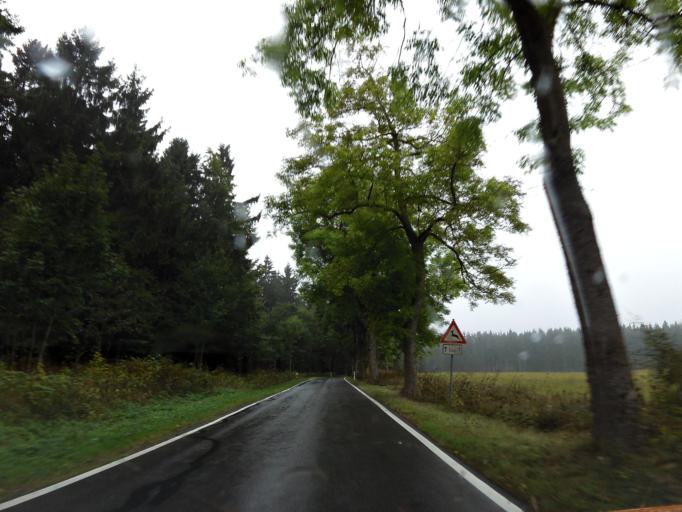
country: DE
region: Saxony-Anhalt
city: Hasselfelde
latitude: 51.6575
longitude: 10.8564
